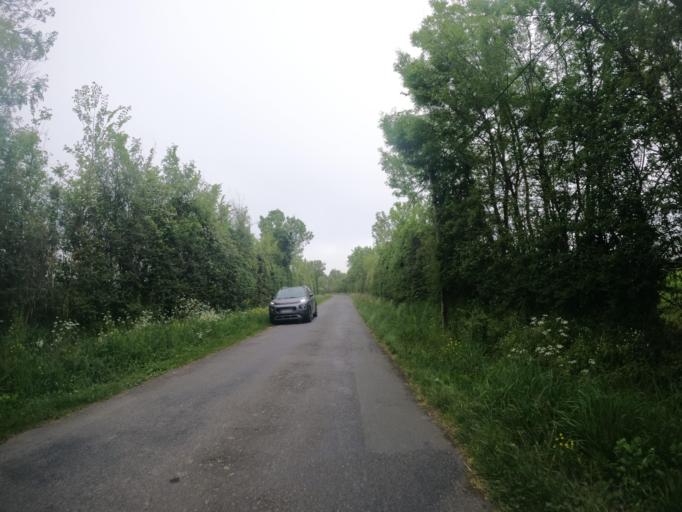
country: FR
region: Poitou-Charentes
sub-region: Departement des Deux-Sevres
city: Chiche
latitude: 46.8877
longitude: -0.3347
